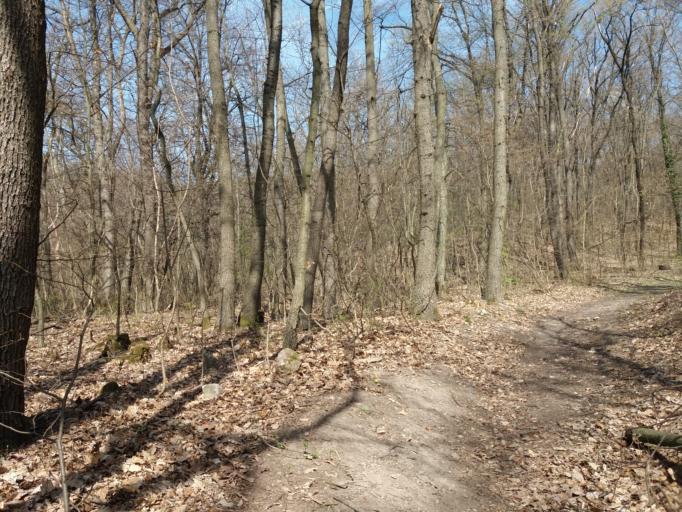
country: HU
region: Pest
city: Csobanka
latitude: 47.6695
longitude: 18.9675
